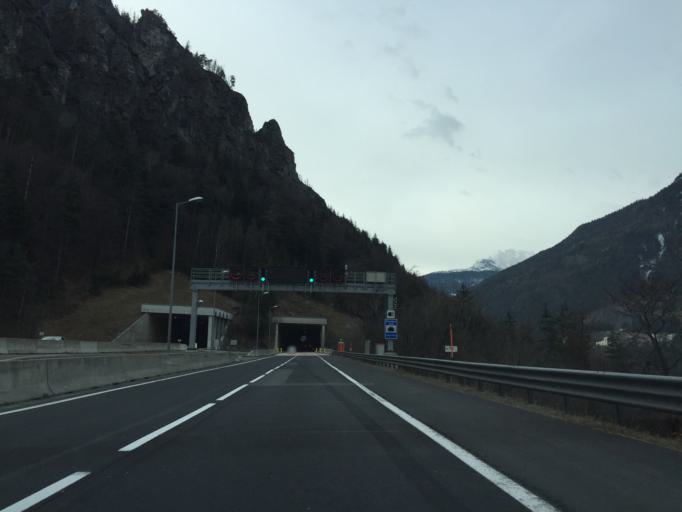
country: AT
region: Salzburg
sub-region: Politischer Bezirk Sankt Johann im Pongau
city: Werfen
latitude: 47.5231
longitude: 13.1691
